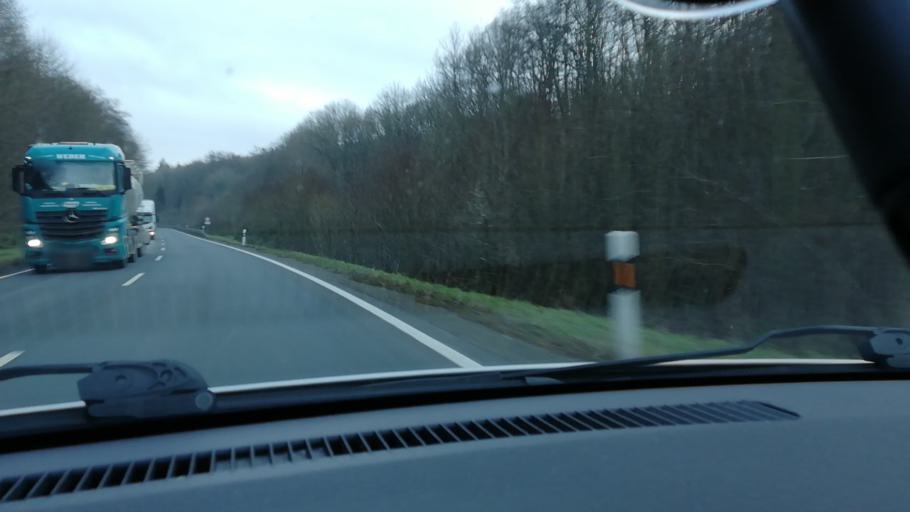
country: DE
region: Bavaria
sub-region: Regierungsbezirk Unterfranken
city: Rechtenbach
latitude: 49.9815
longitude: 9.4894
